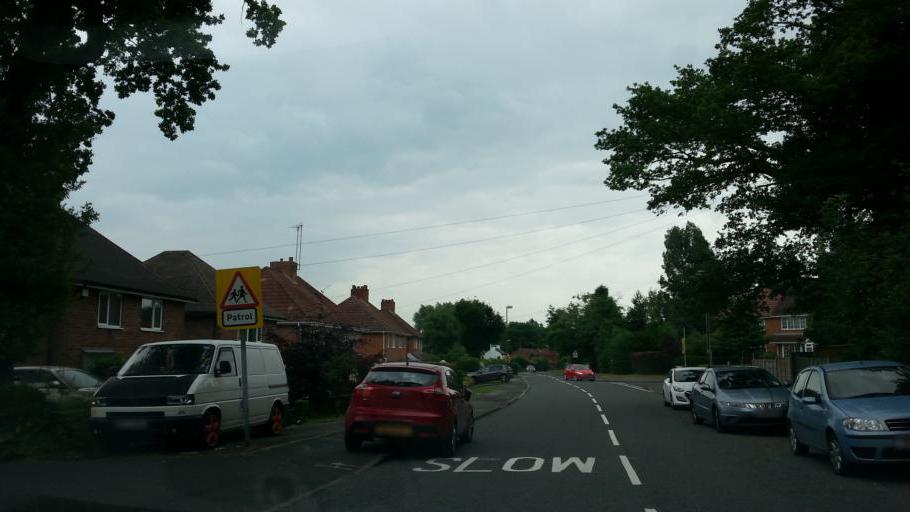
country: GB
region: England
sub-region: Worcestershire
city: Barnt Green
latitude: 52.3914
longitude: -2.0232
